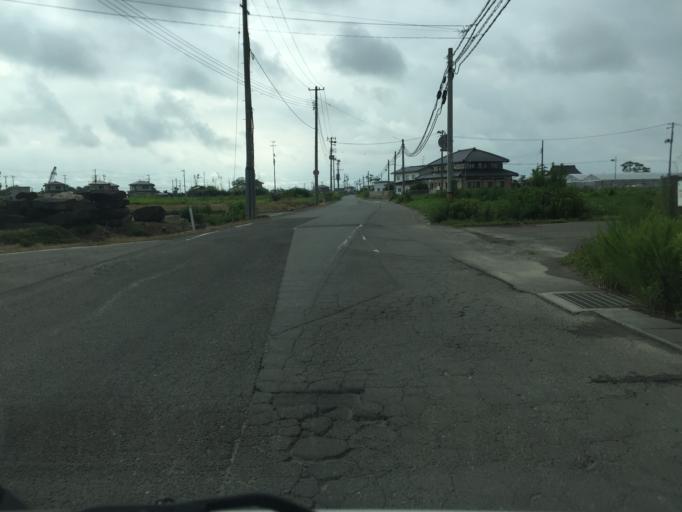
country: JP
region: Miyagi
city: Watari
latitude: 38.0303
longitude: 140.8910
